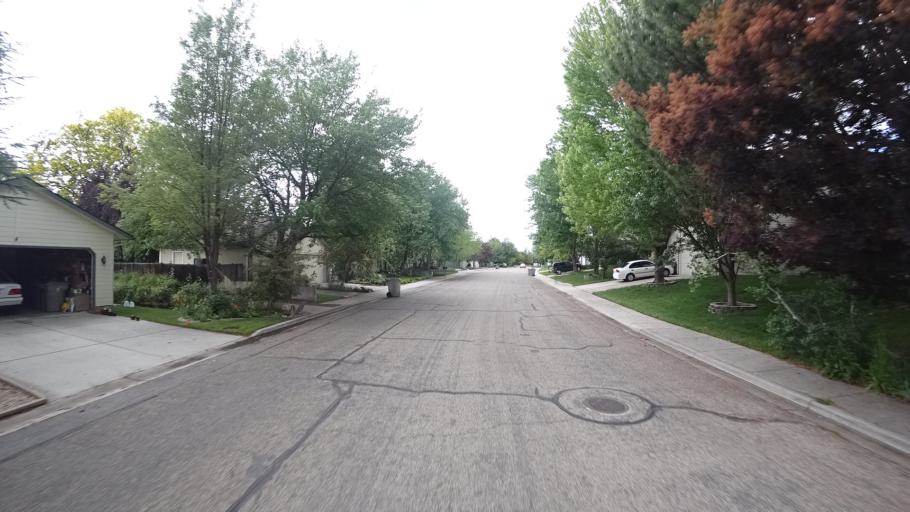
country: US
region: Idaho
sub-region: Ada County
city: Garden City
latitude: 43.6716
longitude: -116.2597
